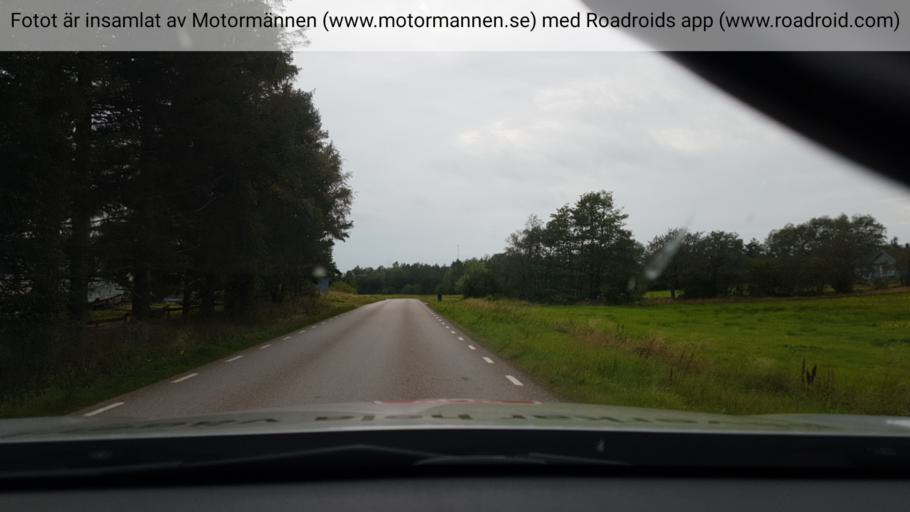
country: SE
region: Vaestra Goetaland
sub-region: Tanums Kommun
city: Grebbestad
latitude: 58.6455
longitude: 11.3000
